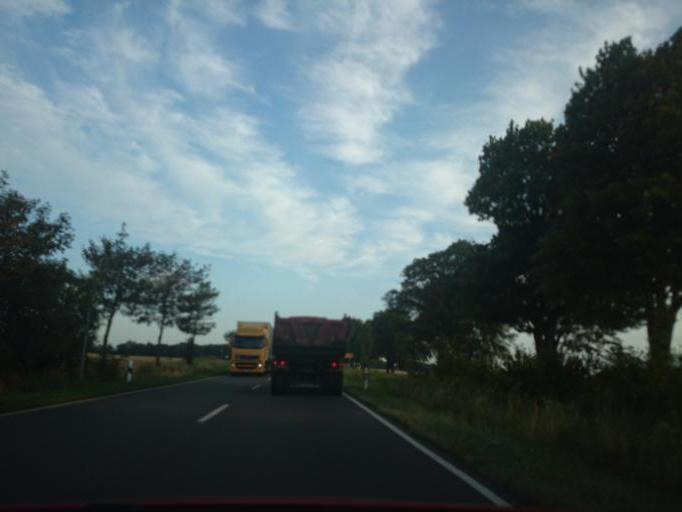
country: DE
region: Mecklenburg-Vorpommern
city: Mesekenhagen
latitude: 54.1914
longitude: 13.2735
